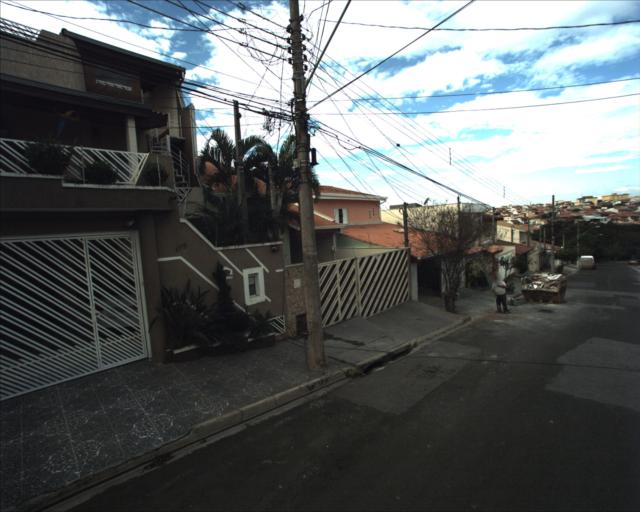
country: BR
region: Sao Paulo
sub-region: Sorocaba
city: Sorocaba
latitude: -23.4889
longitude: -47.5104
